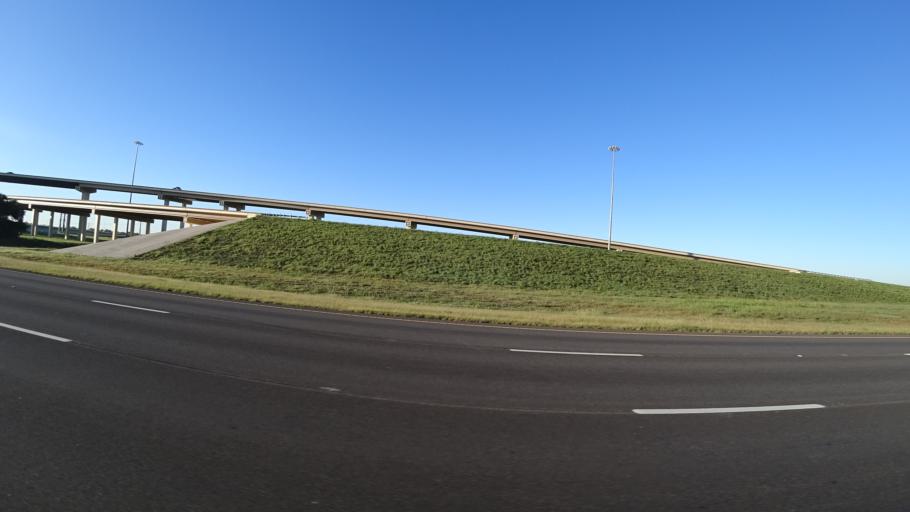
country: US
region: Texas
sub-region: Travis County
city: Hornsby Bend
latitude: 30.1977
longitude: -97.6276
